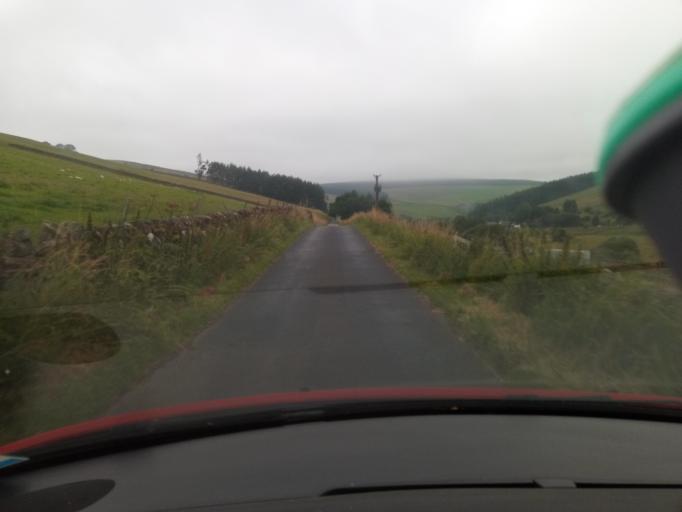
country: GB
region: Scotland
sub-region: The Scottish Borders
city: Galashiels
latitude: 55.6969
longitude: -2.8785
